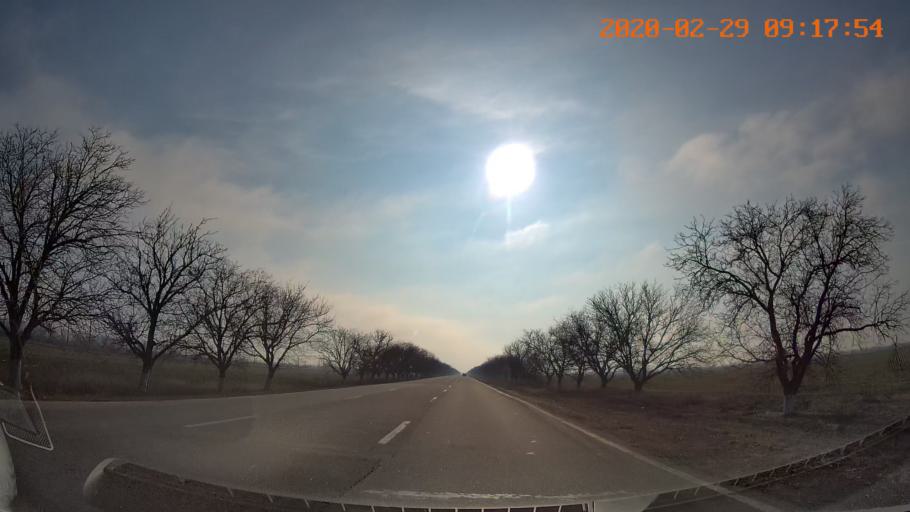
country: MD
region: Telenesti
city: Pervomaisc
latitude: 46.7786
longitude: 29.9128
